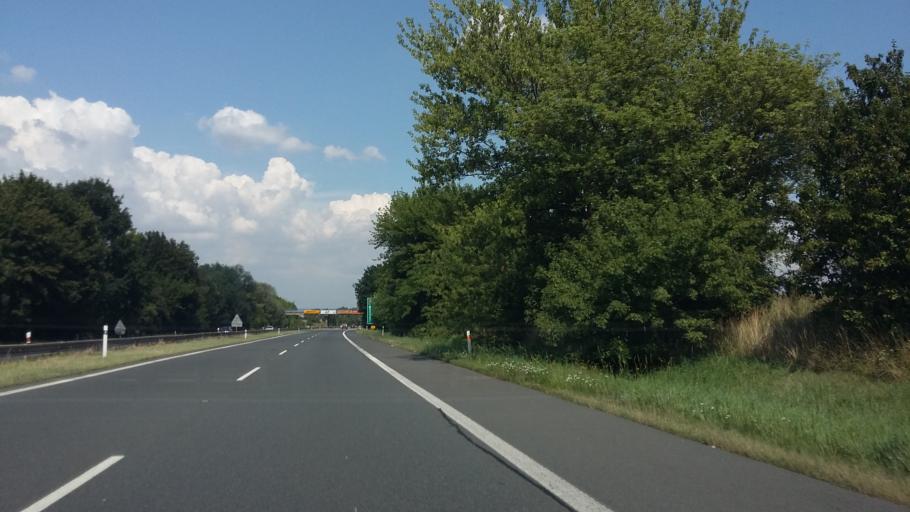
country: CZ
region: Central Bohemia
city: Brandys nad Labem-Stara Boleslav
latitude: 50.1642
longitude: 14.6681
